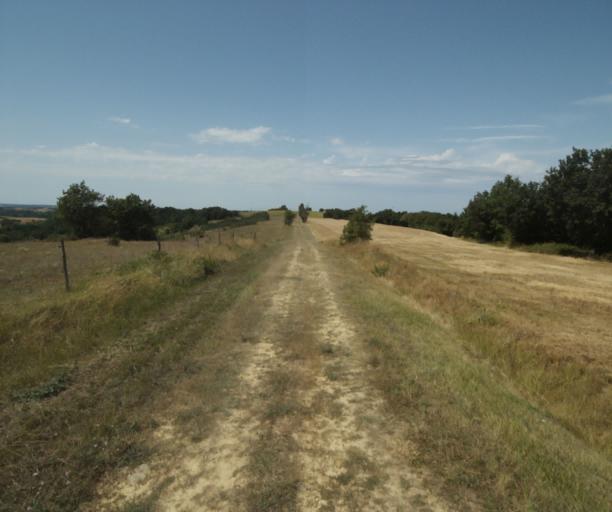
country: FR
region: Midi-Pyrenees
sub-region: Departement de la Haute-Garonne
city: Saint-Felix-Lauragais
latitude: 43.4433
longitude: 1.8659
